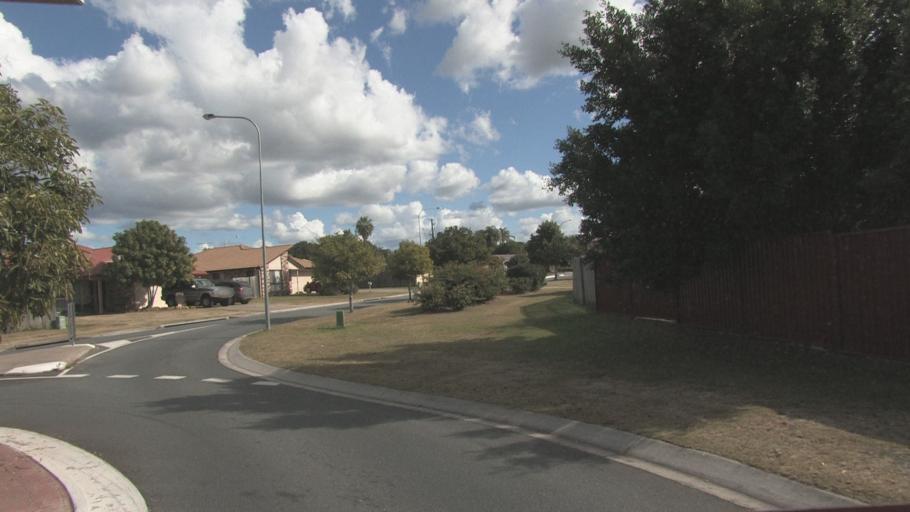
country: AU
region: Queensland
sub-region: Logan
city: Logan Reserve
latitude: -27.6939
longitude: 153.0835
